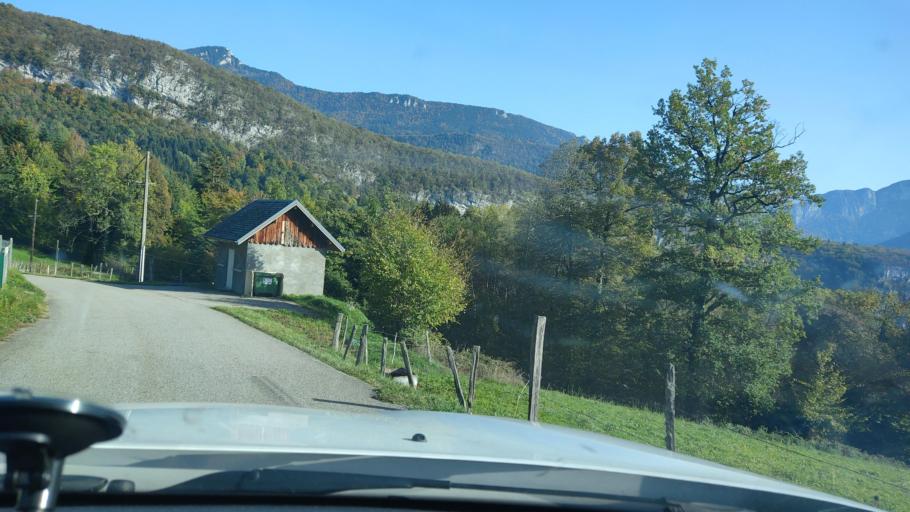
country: FR
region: Rhone-Alpes
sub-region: Departement de la Savoie
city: Les Echelles
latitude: 45.4585
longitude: 5.7762
